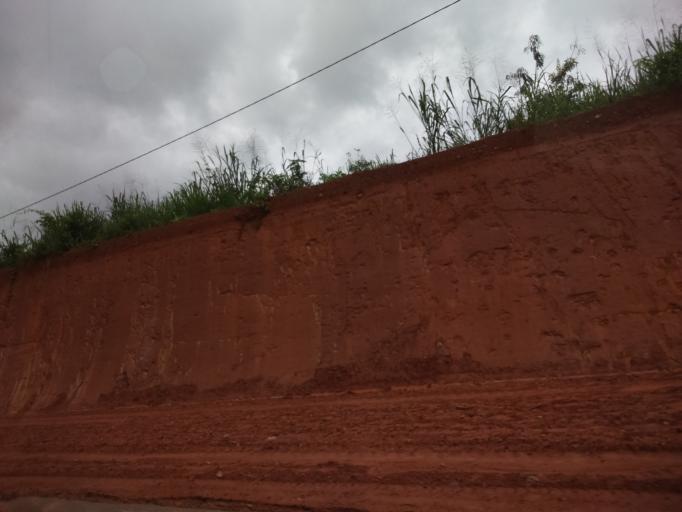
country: CI
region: Moyen-Comoe
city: Abengourou
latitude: 6.6273
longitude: -3.7108
